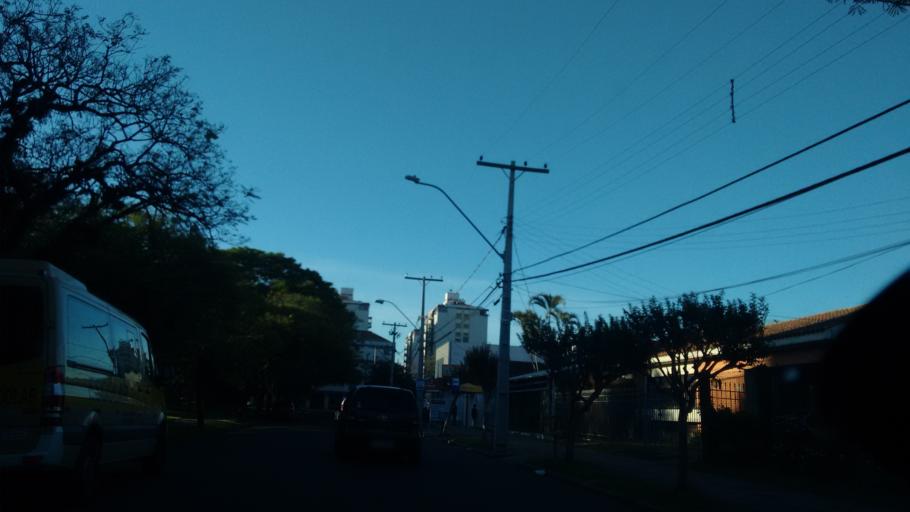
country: BR
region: Rio Grande do Sul
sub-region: Cachoeirinha
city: Cachoeirinha
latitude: -30.0050
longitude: -51.1519
